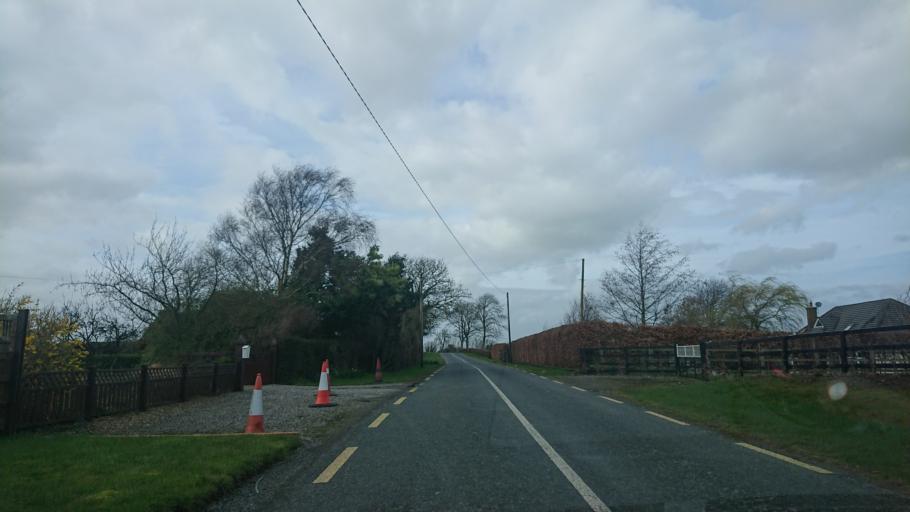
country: IE
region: Leinster
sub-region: Kildare
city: Naas
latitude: 53.1914
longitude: -6.6466
